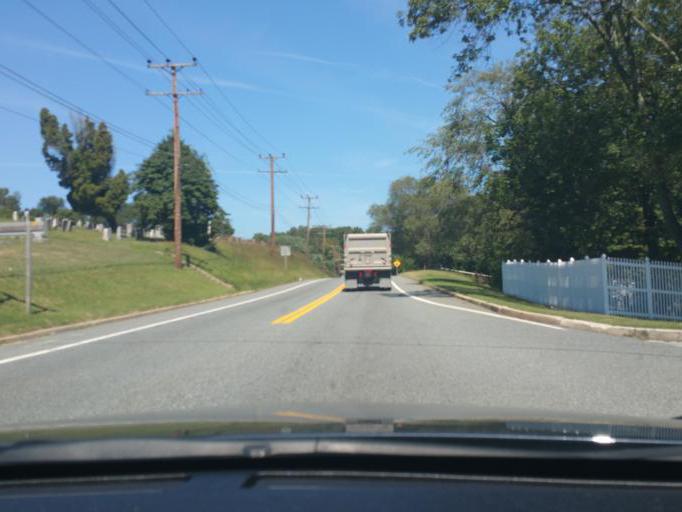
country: US
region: Maryland
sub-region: Harford County
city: Havre de Grace
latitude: 39.5550
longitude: -76.1021
